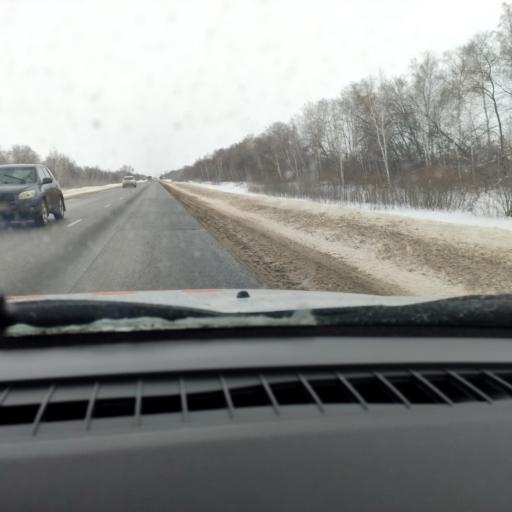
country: RU
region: Samara
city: Dubovyy Umet
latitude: 52.8790
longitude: 50.4305
